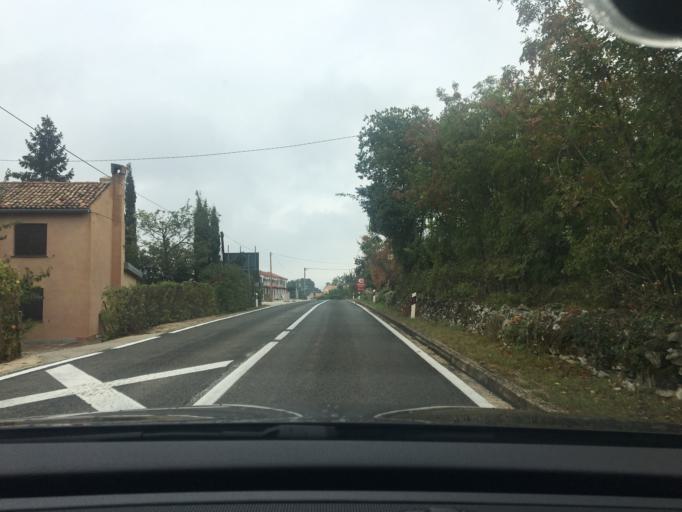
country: HR
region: Istarska
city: Buje
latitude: 45.4442
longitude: 13.6559
